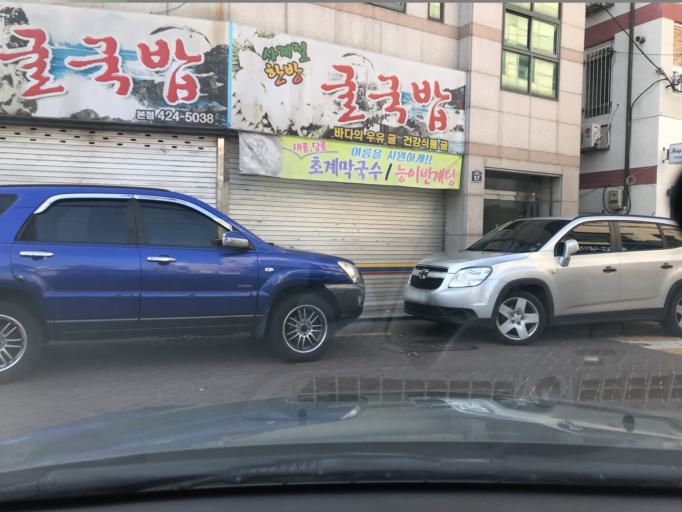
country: KR
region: Daegu
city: Daegu
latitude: 35.8688
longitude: 128.5895
